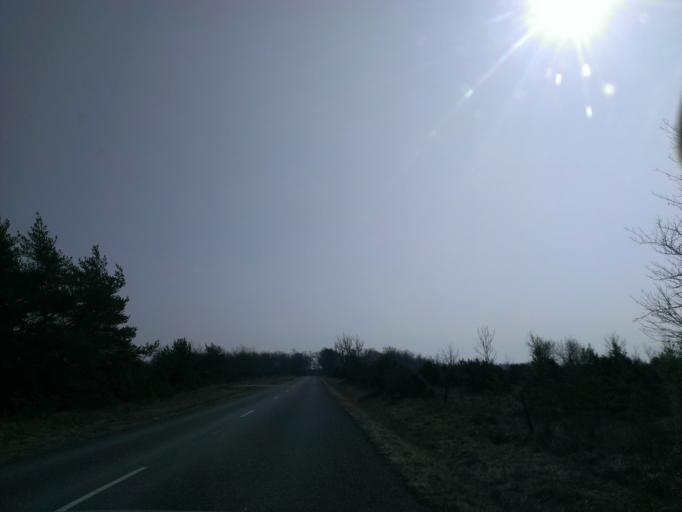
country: EE
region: Saare
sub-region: Kuressaare linn
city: Kuressaare
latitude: 58.2508
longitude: 22.5612
